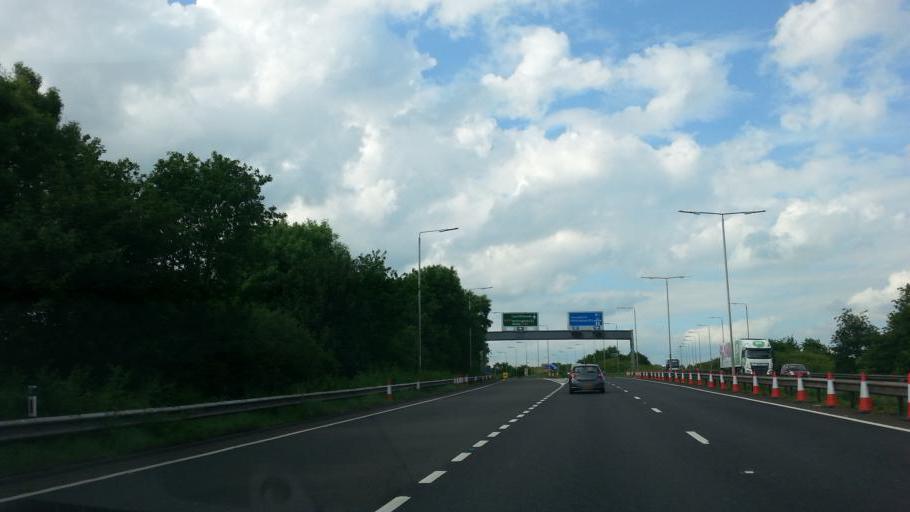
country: GB
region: England
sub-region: Leicestershire
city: Kegworth
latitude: 52.8132
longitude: -1.3099
